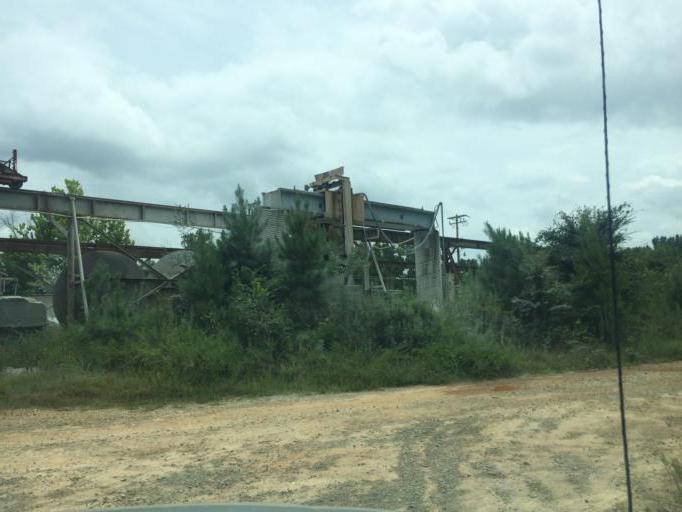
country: US
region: Georgia
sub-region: Elbert County
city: Elberton
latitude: 34.1311
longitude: -82.8626
